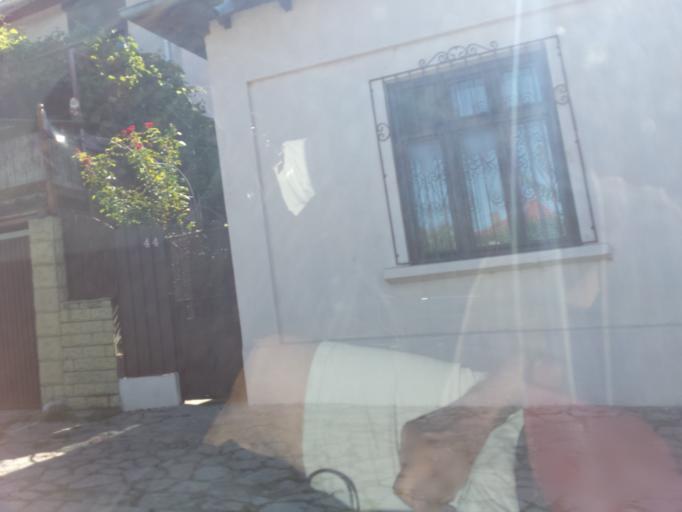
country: RO
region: Tulcea
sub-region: Municipiul Tulcea
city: Tulcea
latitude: 45.1836
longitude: 28.8110
